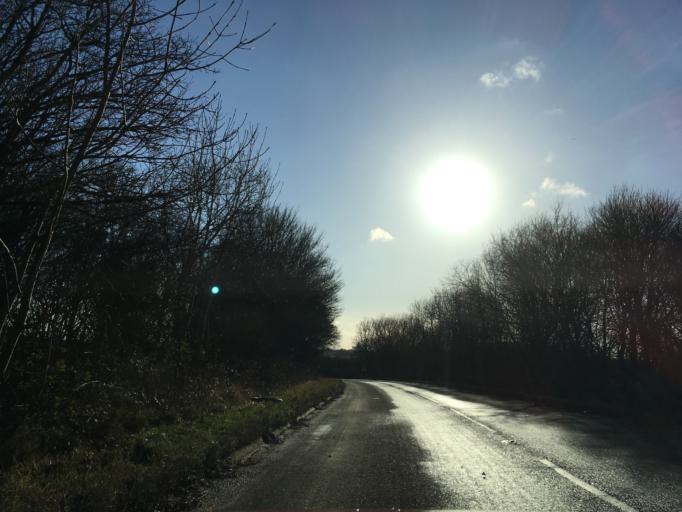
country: GB
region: England
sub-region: Wiltshire
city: Nettleton
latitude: 51.5176
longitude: -2.2733
